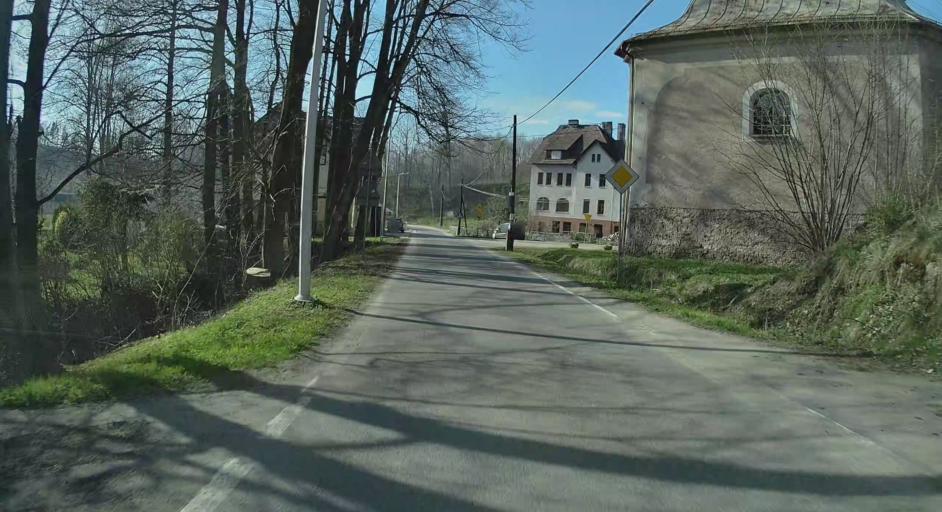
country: PL
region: Lower Silesian Voivodeship
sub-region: Powiat klodzki
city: Lewin Klodzki
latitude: 50.3961
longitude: 16.3005
